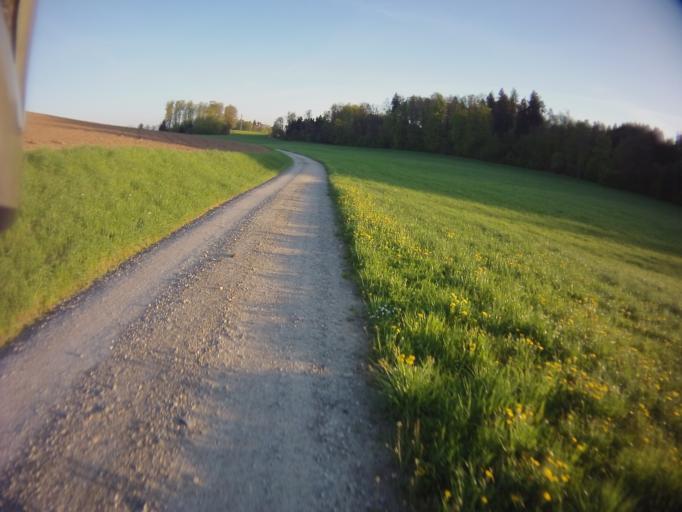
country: CH
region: Zurich
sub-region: Bezirk Affoltern
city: Mettmenstetten
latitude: 47.2436
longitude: 8.4522
